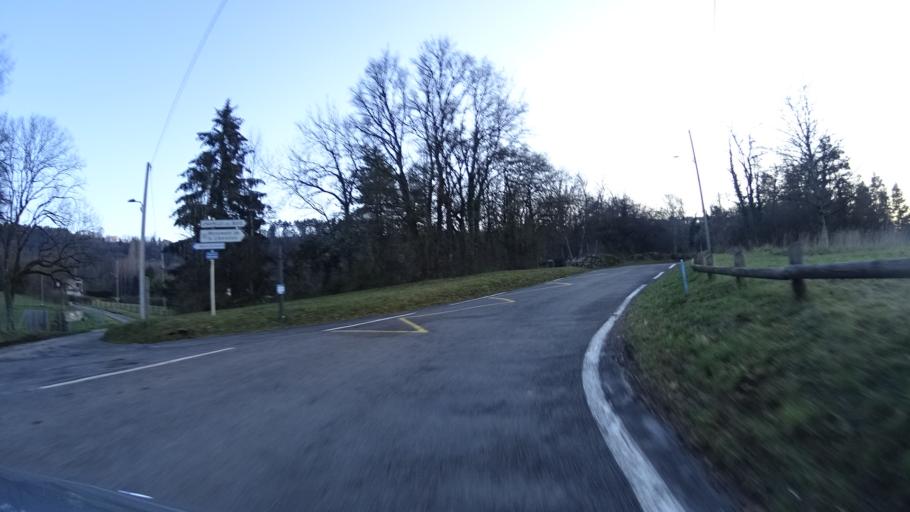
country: FR
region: Franche-Comte
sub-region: Departement du Doubs
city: Morre
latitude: 47.2225
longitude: 6.0430
